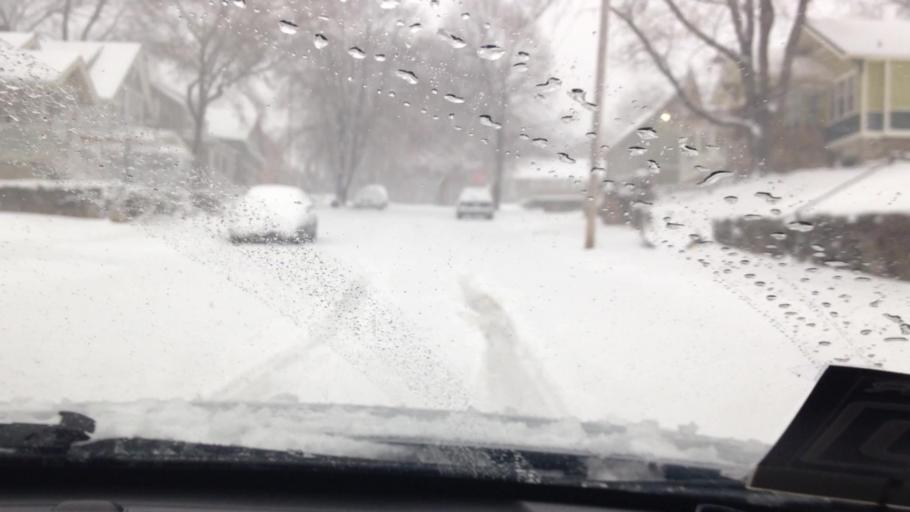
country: US
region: Kansas
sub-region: Johnson County
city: Westwood
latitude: 39.0419
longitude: -94.6035
